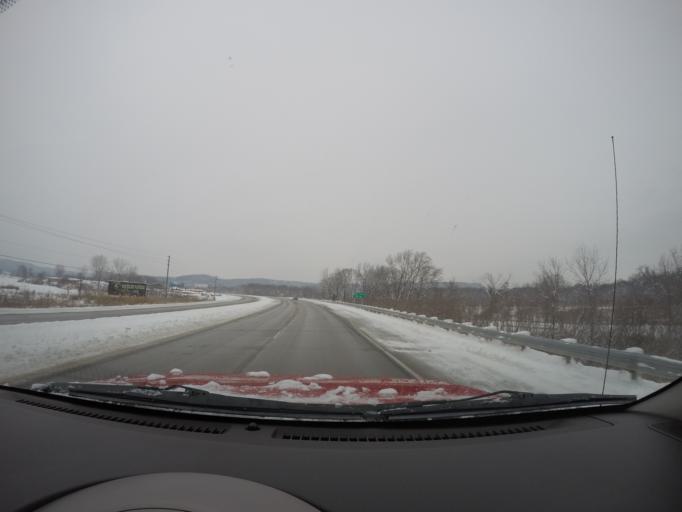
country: US
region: Minnesota
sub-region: Houston County
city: La Crescent
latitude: 43.8245
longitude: -91.2832
